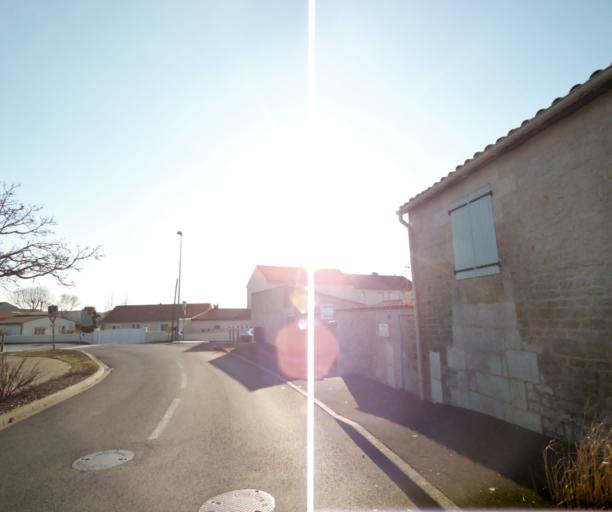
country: FR
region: Poitou-Charentes
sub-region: Departement des Deux-Sevres
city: Niort
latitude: 46.3418
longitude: -0.4577
